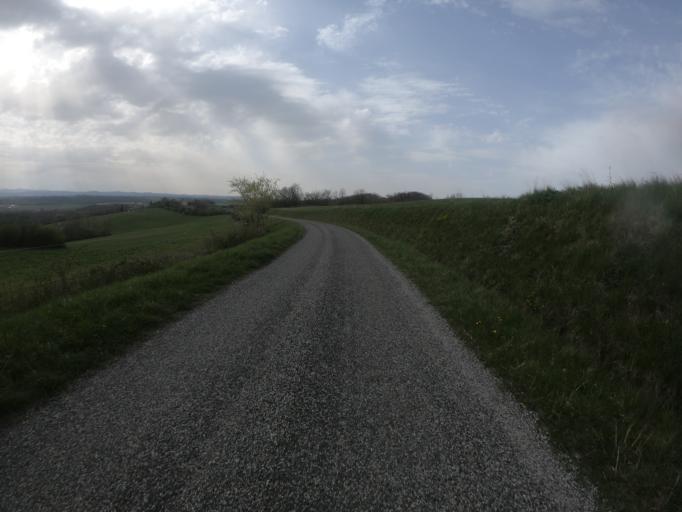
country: FR
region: Languedoc-Roussillon
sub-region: Departement de l'Aude
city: Belpech
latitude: 43.1317
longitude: 1.7580
